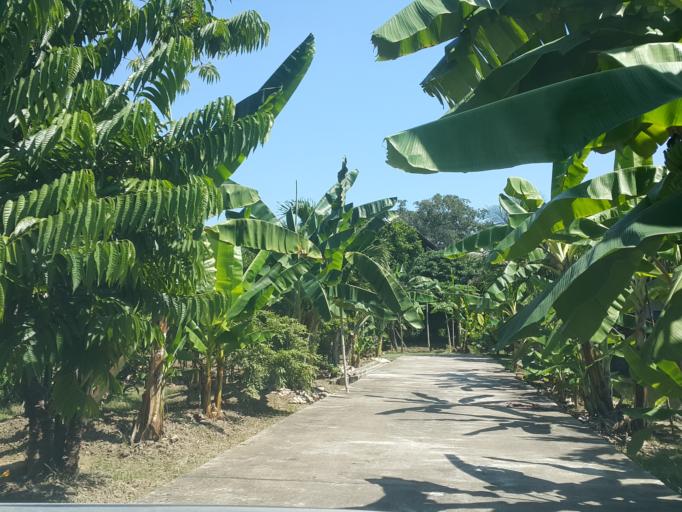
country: TH
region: Chiang Mai
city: Saraphi
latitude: 18.7631
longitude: 99.0485
